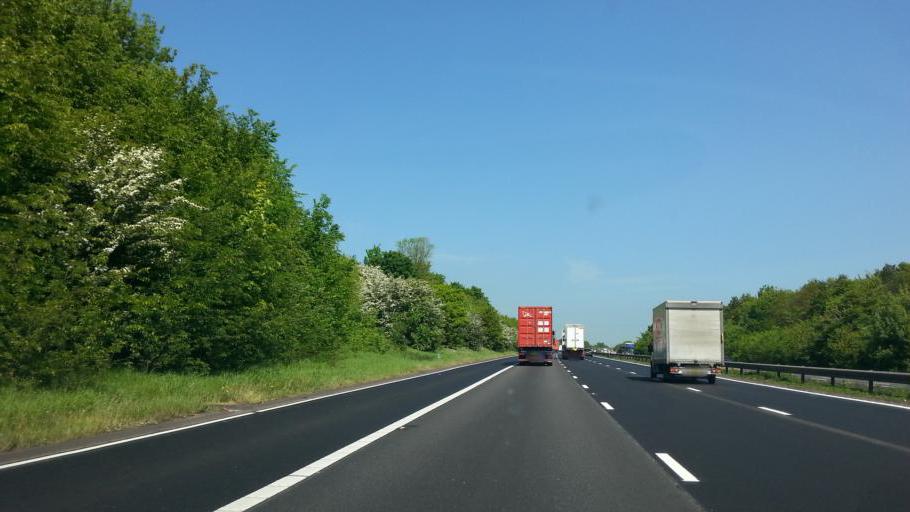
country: GB
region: England
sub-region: Gloucestershire
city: Uckington
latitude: 51.9579
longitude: -2.1282
